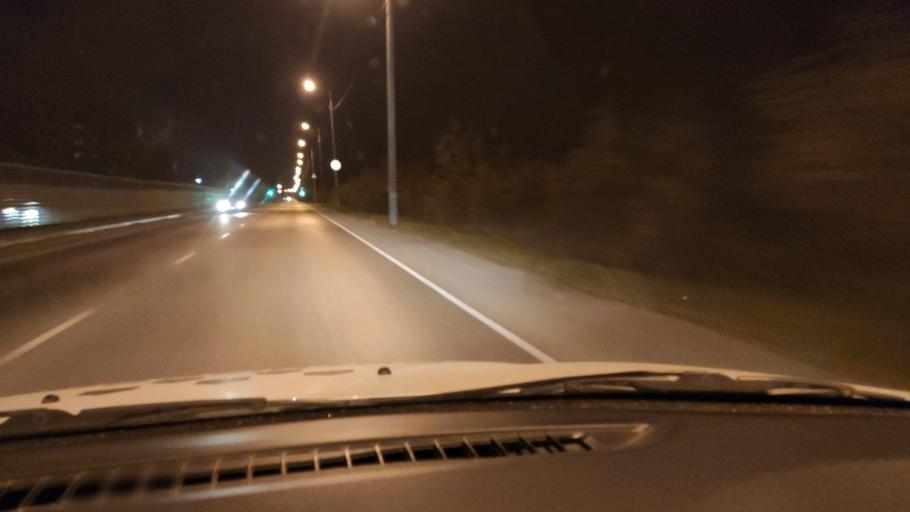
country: RU
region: Perm
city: Kondratovo
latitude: 57.9793
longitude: 56.1306
